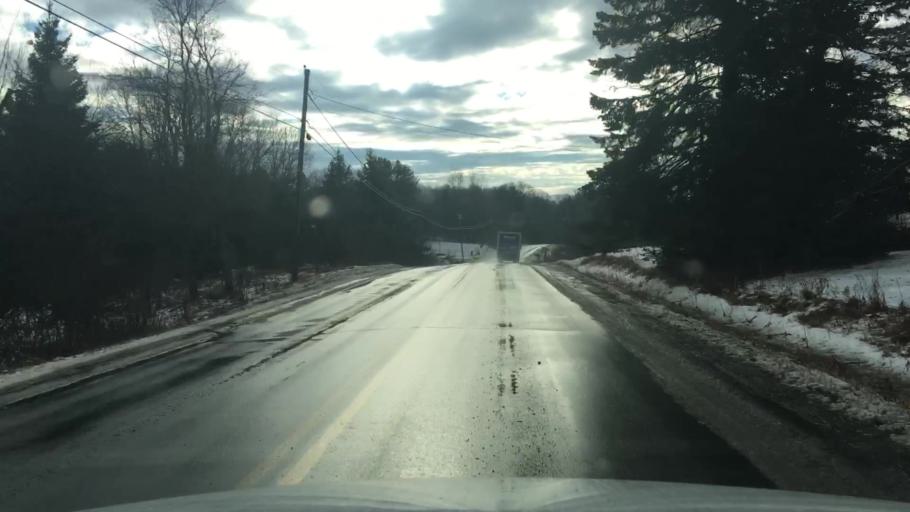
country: US
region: Maine
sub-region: Penobscot County
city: Brewer
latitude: 44.7429
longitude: -68.7655
